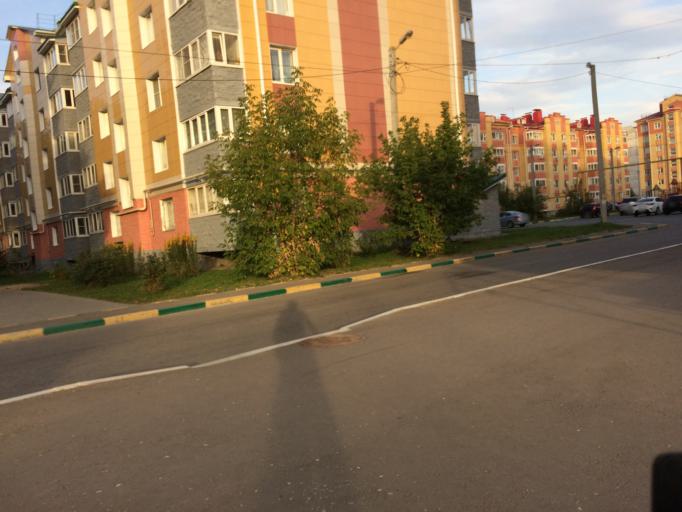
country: RU
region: Mariy-El
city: Yoshkar-Ola
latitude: 56.6301
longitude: 47.8494
